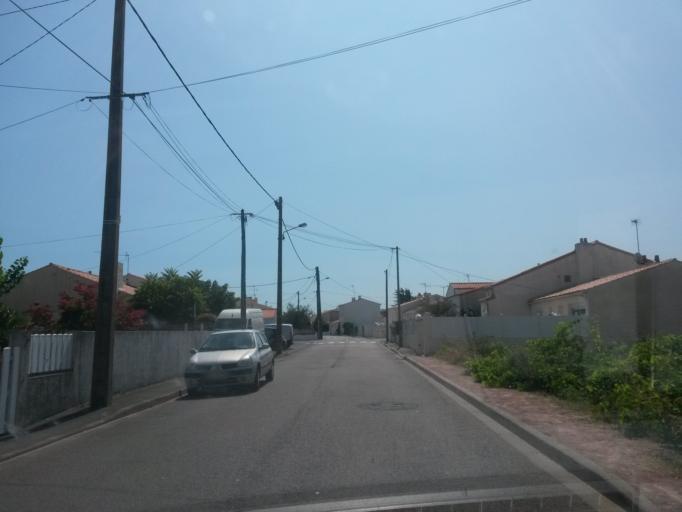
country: FR
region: Pays de la Loire
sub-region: Departement de la Vendee
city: Les Sables-d'Olonne
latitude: 46.5086
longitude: -1.8068
